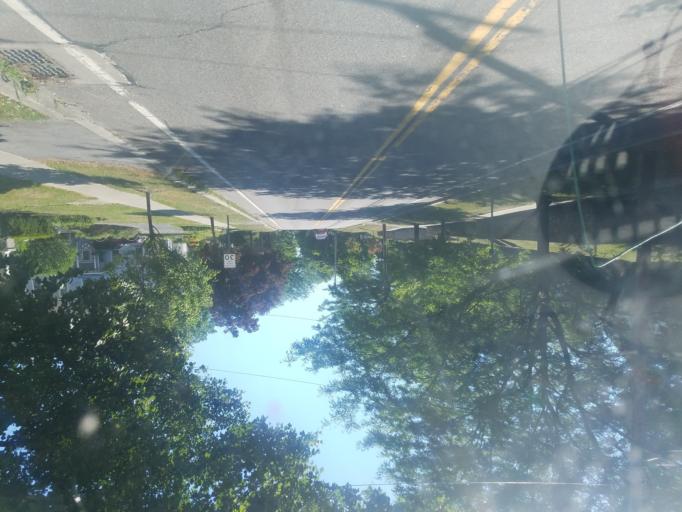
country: US
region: New York
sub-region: Ontario County
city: Phelps
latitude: 42.9556
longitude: -77.0517
